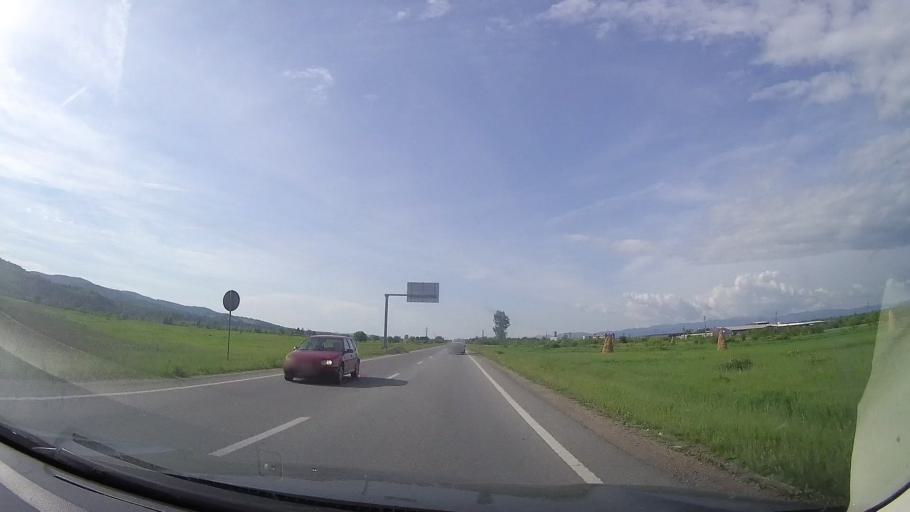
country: RO
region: Caras-Severin
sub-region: Comuna Buchin
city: Buchin
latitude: 45.3707
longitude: 22.2385
